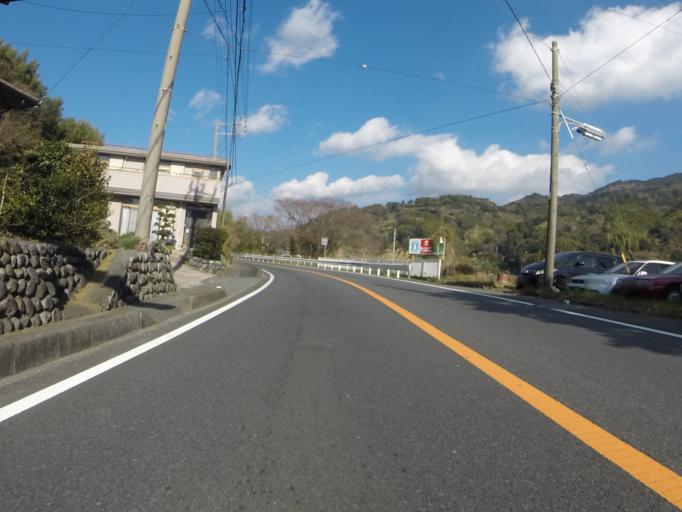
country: JP
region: Shizuoka
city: Fujinomiya
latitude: 35.0781
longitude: 138.5210
